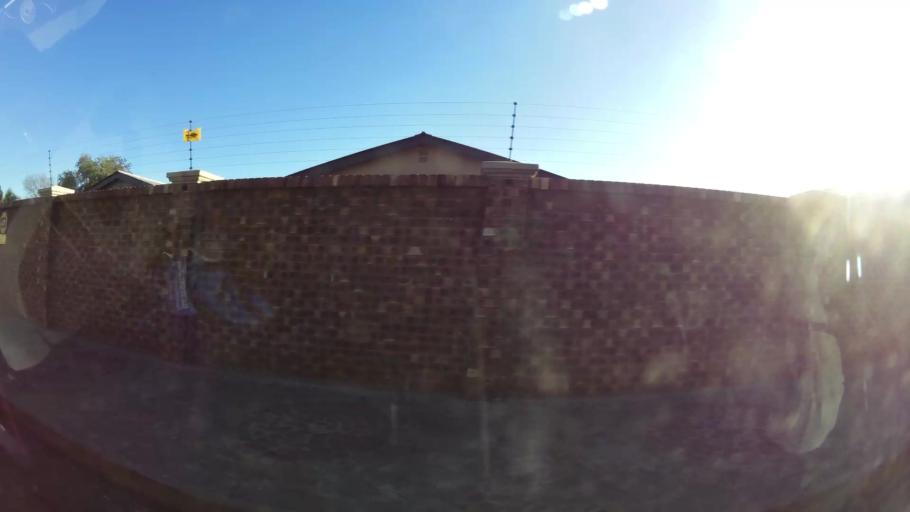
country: ZA
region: Northern Cape
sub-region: Frances Baard District Municipality
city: Kimberley
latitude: -28.7372
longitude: 24.7316
